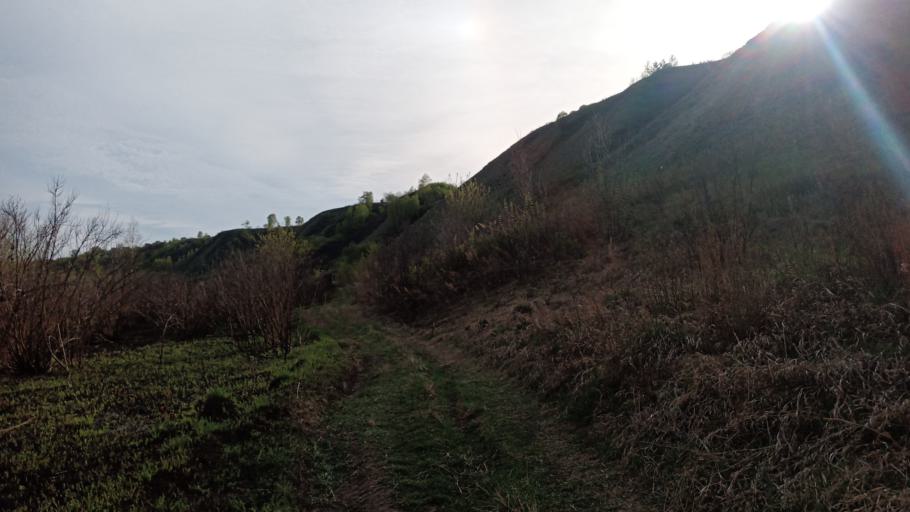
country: RU
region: Altai Krai
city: Yuzhnyy
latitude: 53.2227
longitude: 83.7260
